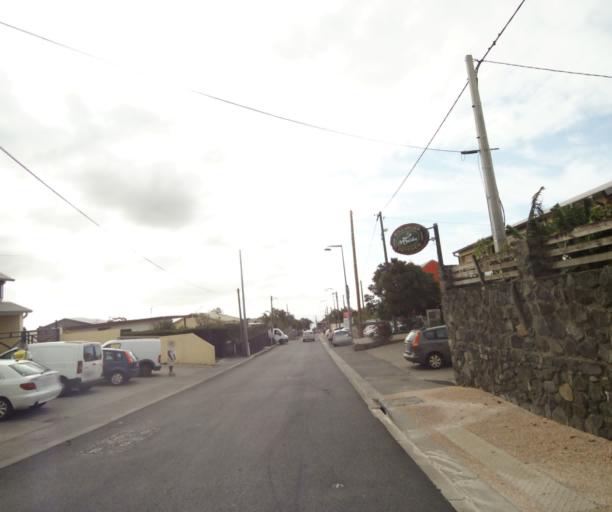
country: RE
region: Reunion
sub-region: Reunion
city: Saint-Paul
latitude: -21.0401
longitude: 55.3003
